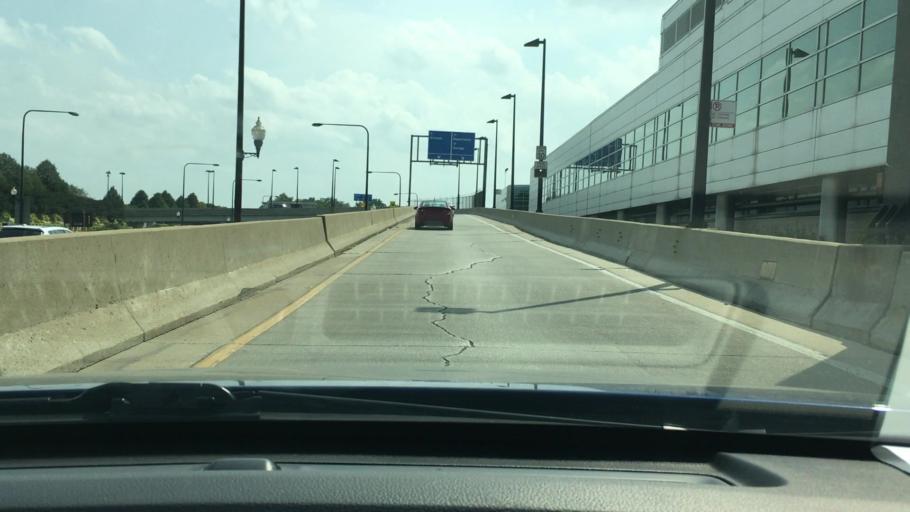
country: US
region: Illinois
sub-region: Cook County
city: Hometown
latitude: 41.7870
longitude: -87.7416
